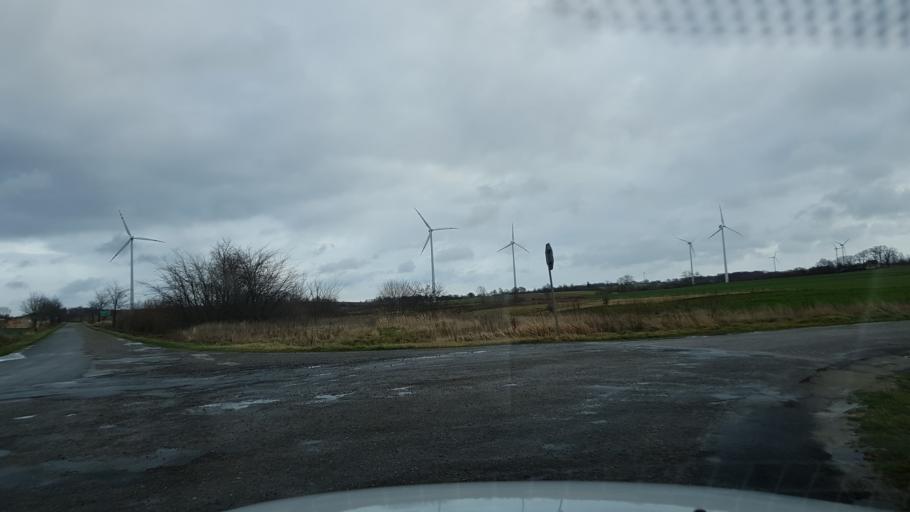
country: PL
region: West Pomeranian Voivodeship
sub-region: Powiat slawienski
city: Slawno
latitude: 54.5184
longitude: 16.6971
